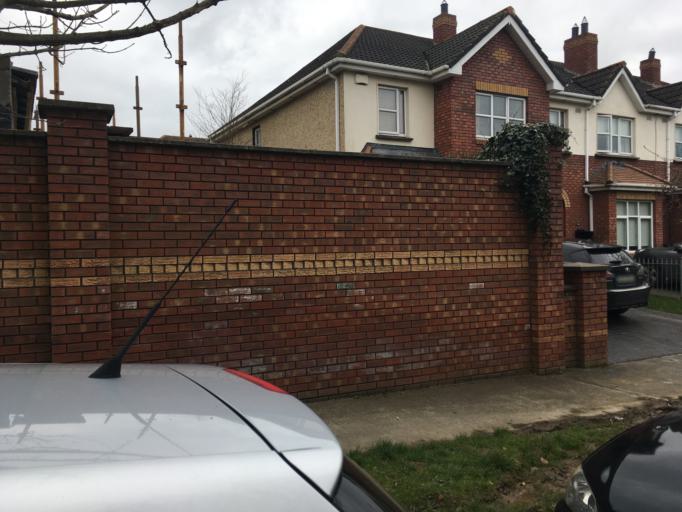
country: IE
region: Leinster
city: Portmarnock
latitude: 53.4363
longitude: -6.1420
